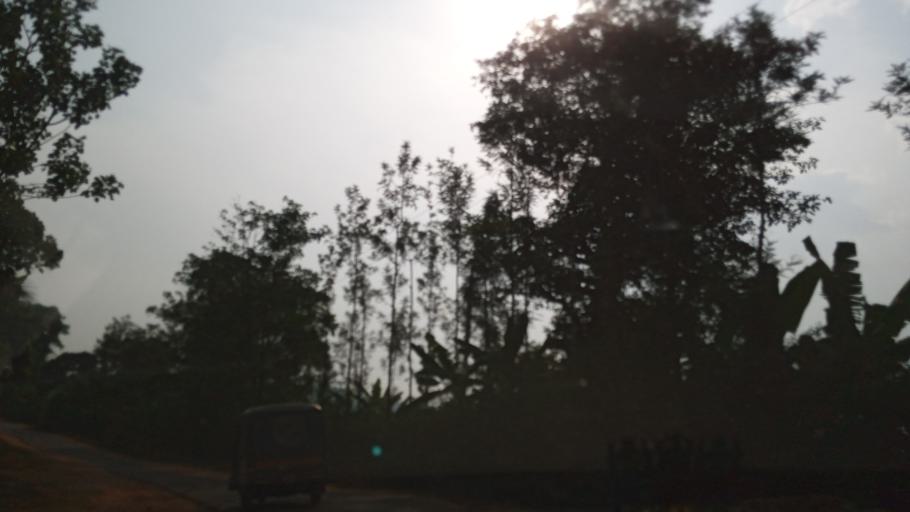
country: IN
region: Karnataka
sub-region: Chikmagalur
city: Mudigere
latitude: 13.0600
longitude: 75.6626
